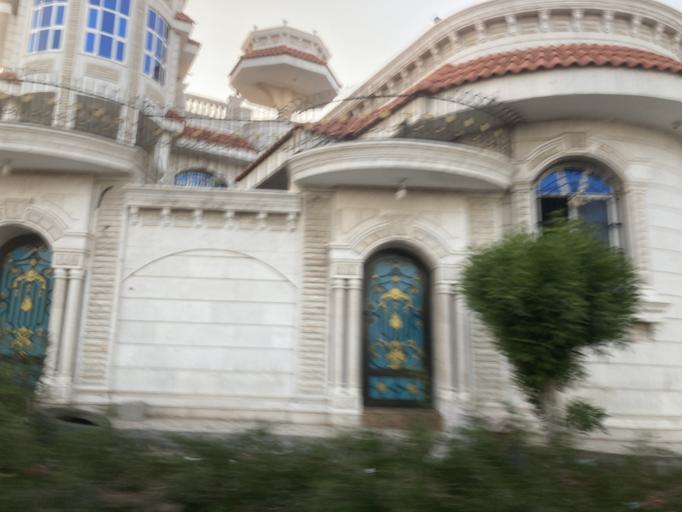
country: YE
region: Aden
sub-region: Al Mansura
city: Al Mansurah
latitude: 12.8523
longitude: 44.9912
